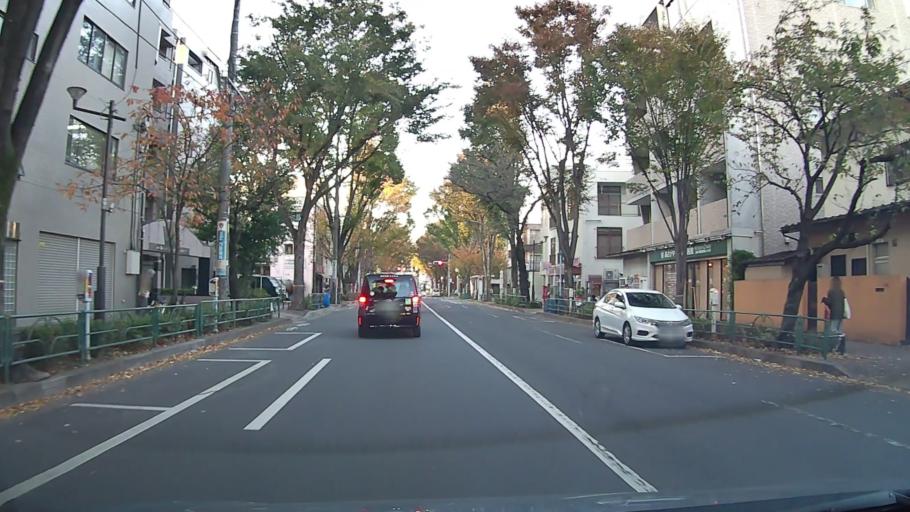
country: JP
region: Tokyo
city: Tokyo
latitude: 35.7118
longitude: 139.6350
